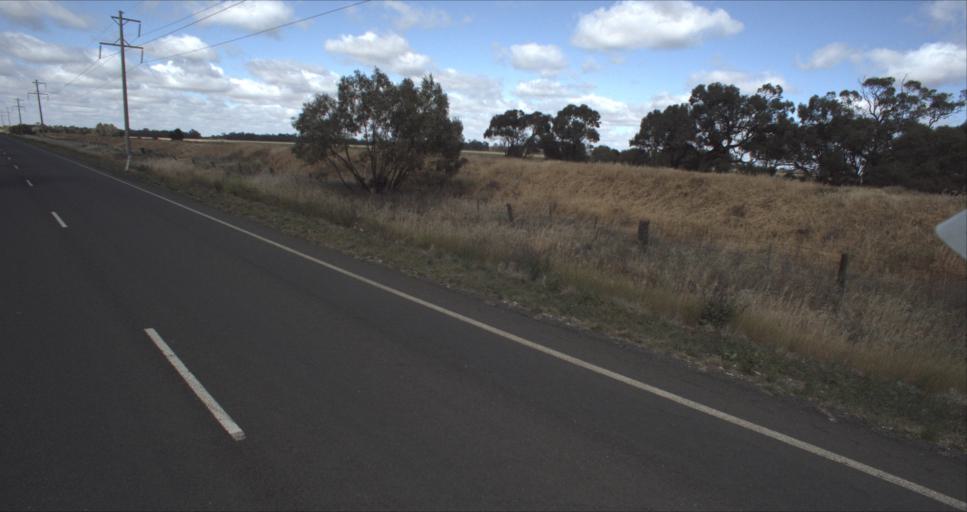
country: AU
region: New South Wales
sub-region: Murrumbidgee Shire
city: Darlington Point
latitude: -34.5310
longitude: 146.1739
